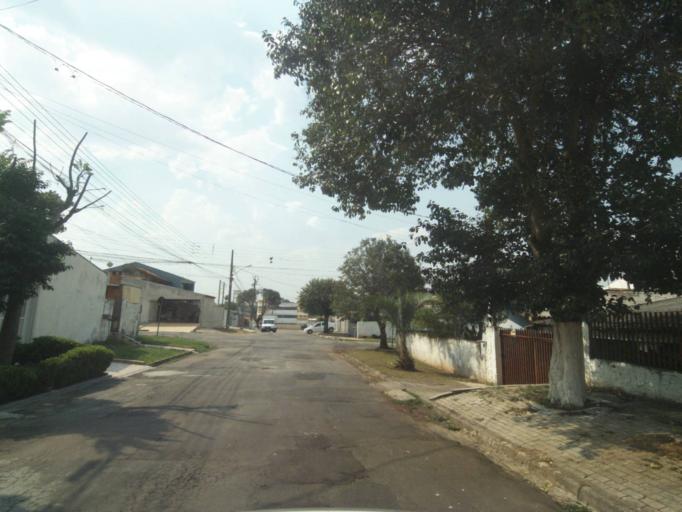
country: BR
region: Parana
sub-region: Sao Jose Dos Pinhais
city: Sao Jose dos Pinhais
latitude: -25.5395
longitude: -49.2383
